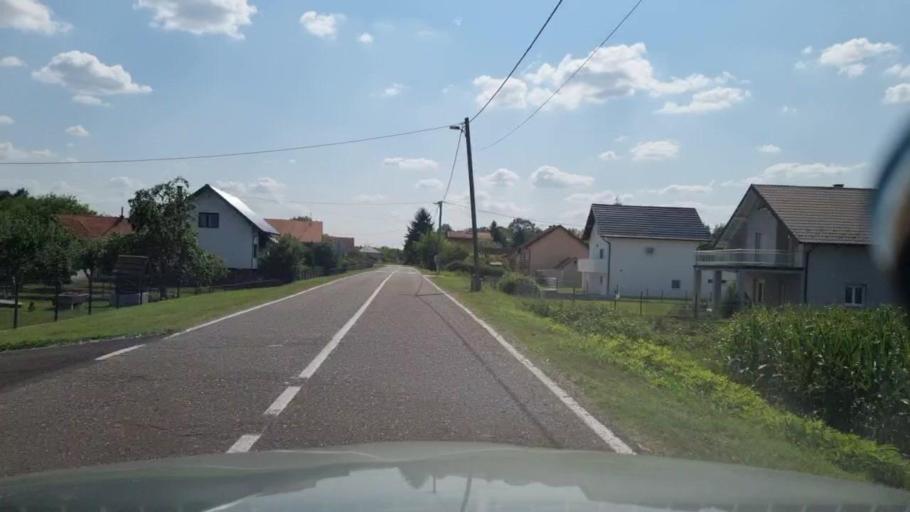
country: BA
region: Federation of Bosnia and Herzegovina
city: Donja Dubica
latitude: 45.0702
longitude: 18.4364
